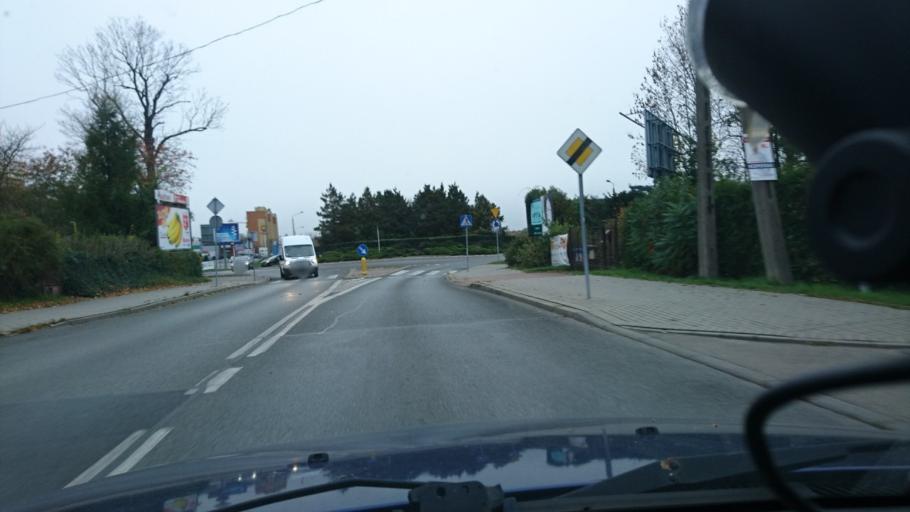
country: PL
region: Silesian Voivodeship
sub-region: Bielsko-Biala
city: Bielsko-Biala
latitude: 49.8124
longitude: 19.0122
